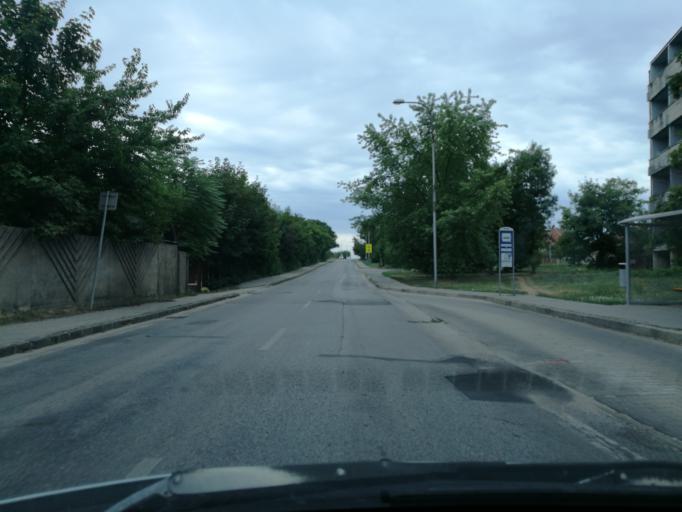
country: SK
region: Nitriansky
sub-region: Okres Nitra
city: Nitra
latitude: 48.2992
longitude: 18.0778
